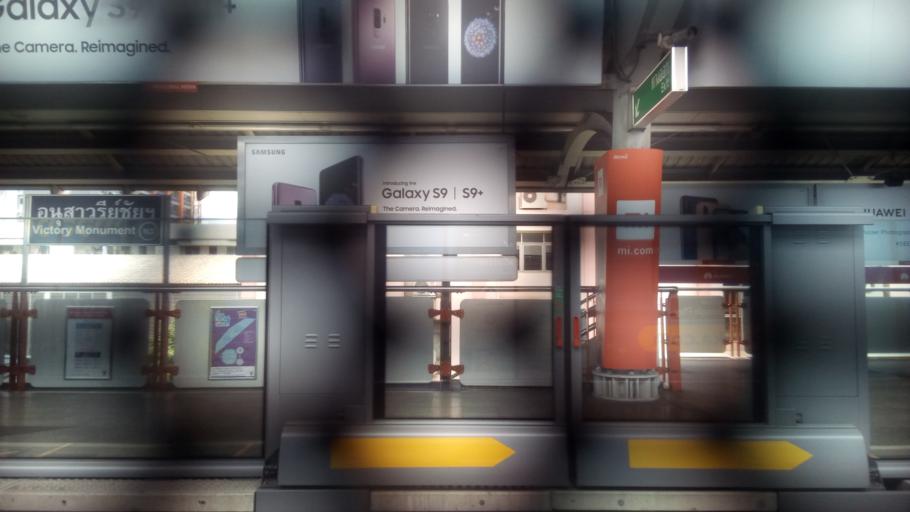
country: TH
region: Bangkok
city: Ratchathewi
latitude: 13.7619
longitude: 100.5366
